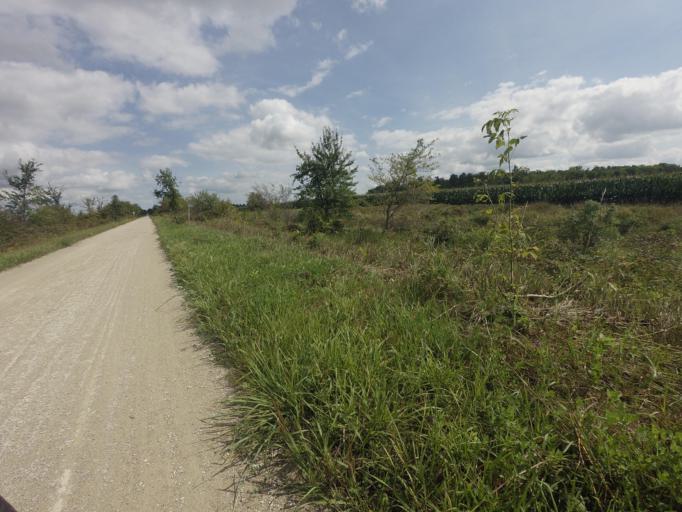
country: CA
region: Ontario
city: North Perth
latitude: 43.5761
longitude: -80.8108
